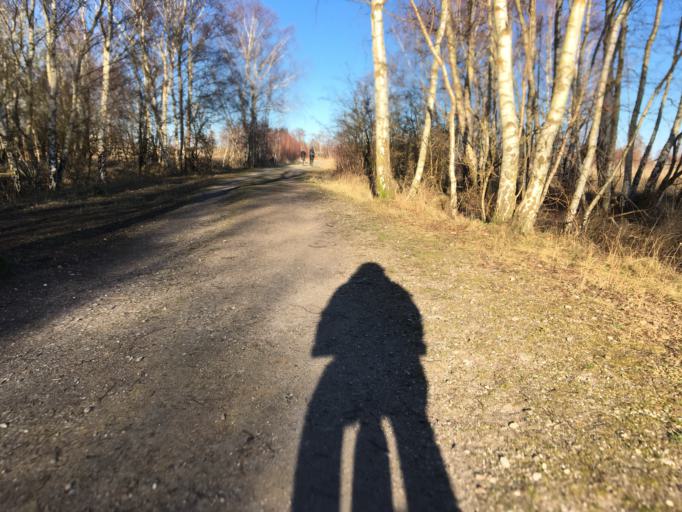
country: DK
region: Capital Region
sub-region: Tarnby Kommune
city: Tarnby
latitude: 55.5903
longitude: 12.5667
